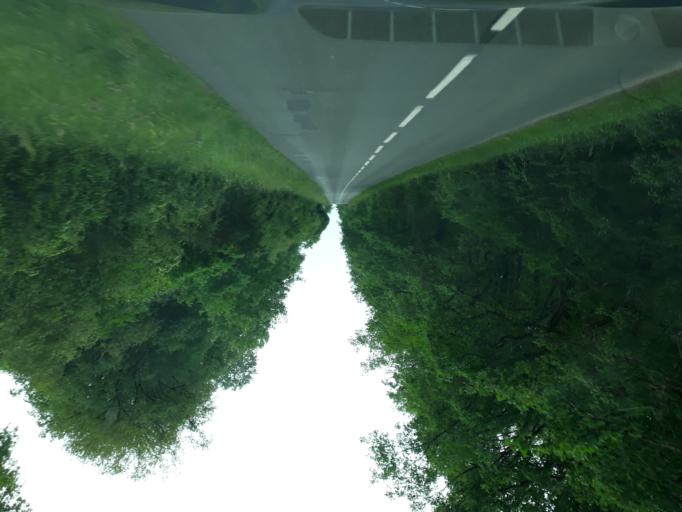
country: FR
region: Centre
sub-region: Departement du Loiret
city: Saint-Pere-sur-Loire
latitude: 47.7454
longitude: 2.3550
